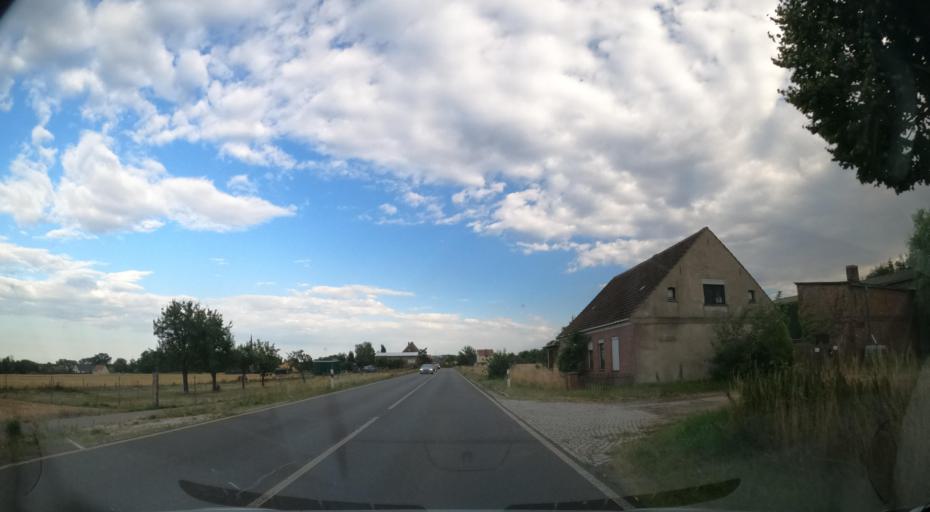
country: DE
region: Mecklenburg-Vorpommern
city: Viereck
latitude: 53.4956
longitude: 14.0843
